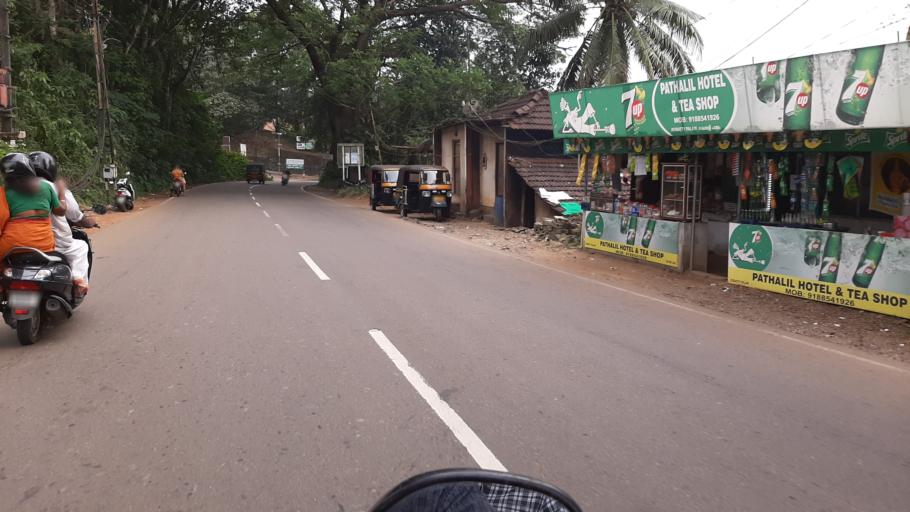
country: IN
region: Kerala
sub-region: Kottayam
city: Erattupetta
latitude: 9.4949
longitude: 76.8494
